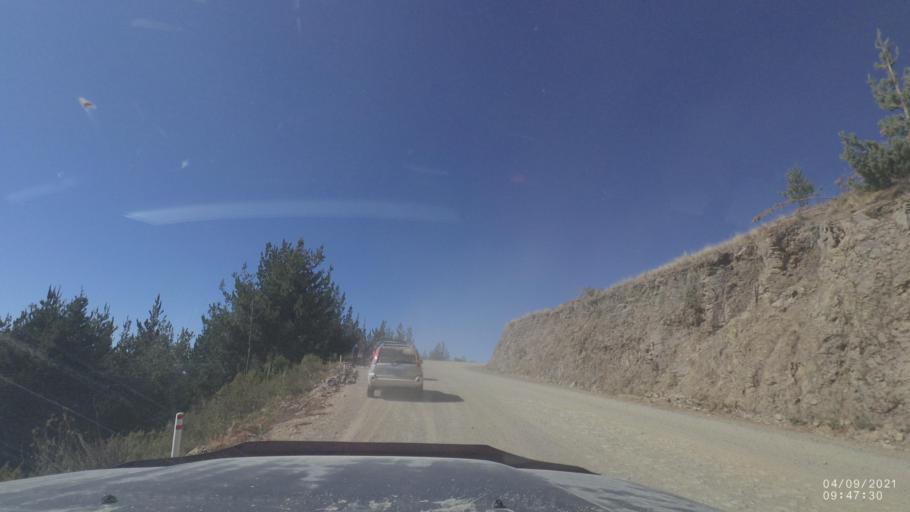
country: BO
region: Cochabamba
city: Sipe Sipe
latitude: -17.3547
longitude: -66.3872
